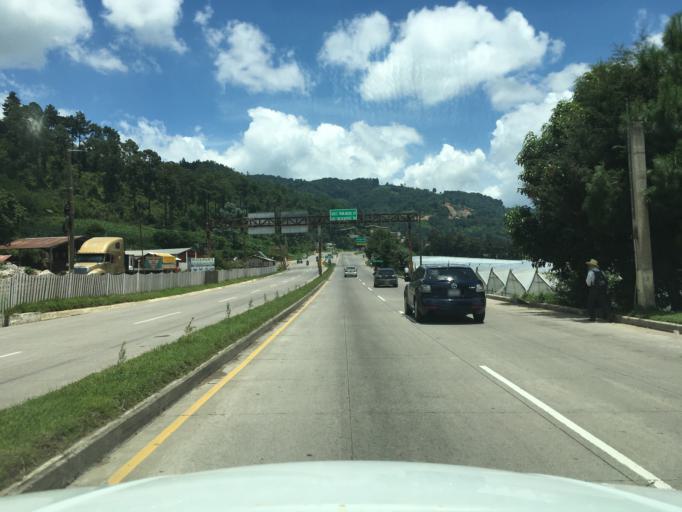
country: GT
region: Chimaltenango
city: Tecpan Guatemala
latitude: 14.7768
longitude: -90.9876
